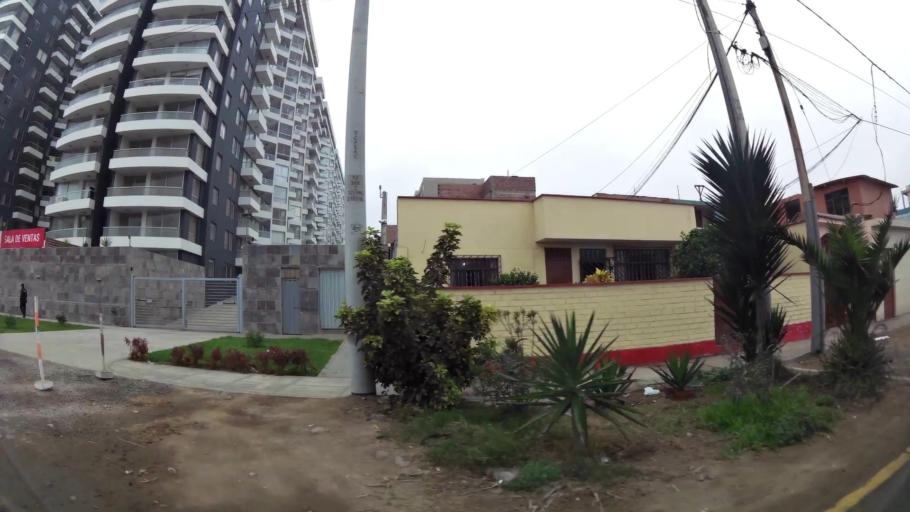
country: PE
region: Callao
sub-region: Callao
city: Callao
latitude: -12.0828
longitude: -77.1037
